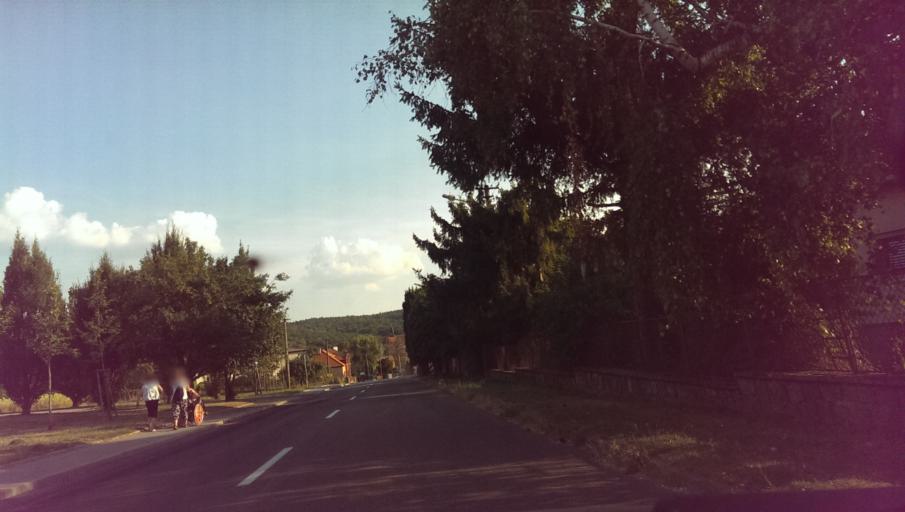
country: CZ
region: Zlin
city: Lukov
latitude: 49.2661
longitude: 17.7158
